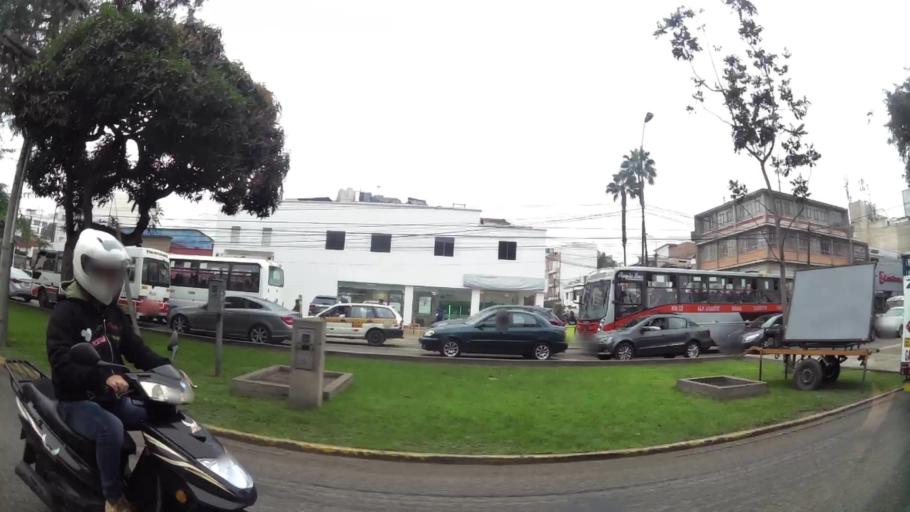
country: PE
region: Lima
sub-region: Lima
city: Surco
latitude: -12.1258
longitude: -77.0213
